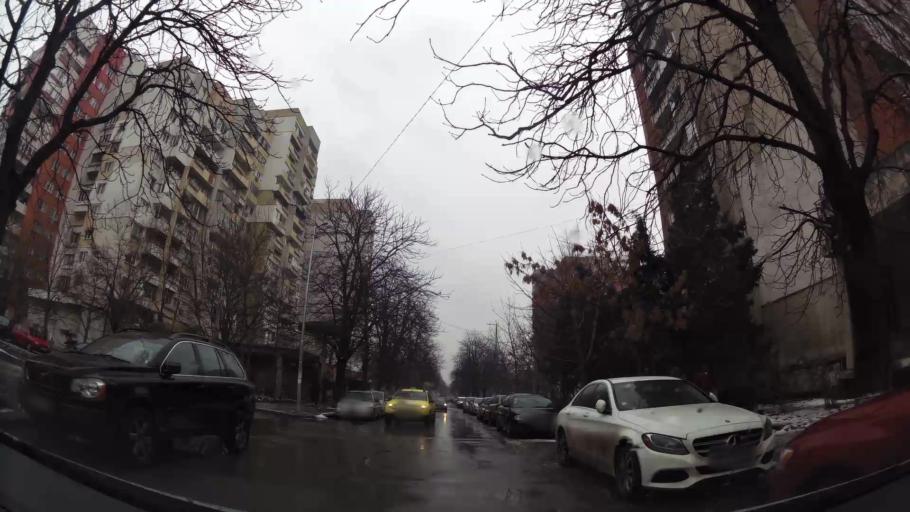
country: BG
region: Sofia-Capital
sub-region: Stolichna Obshtina
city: Sofia
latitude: 42.6759
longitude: 23.2947
